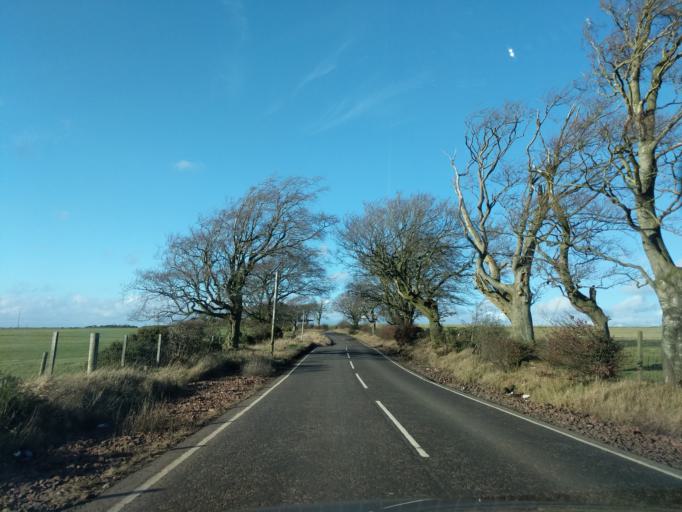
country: GB
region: Scotland
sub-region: South Lanarkshire
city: Carluke
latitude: 55.7589
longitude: -3.8407
